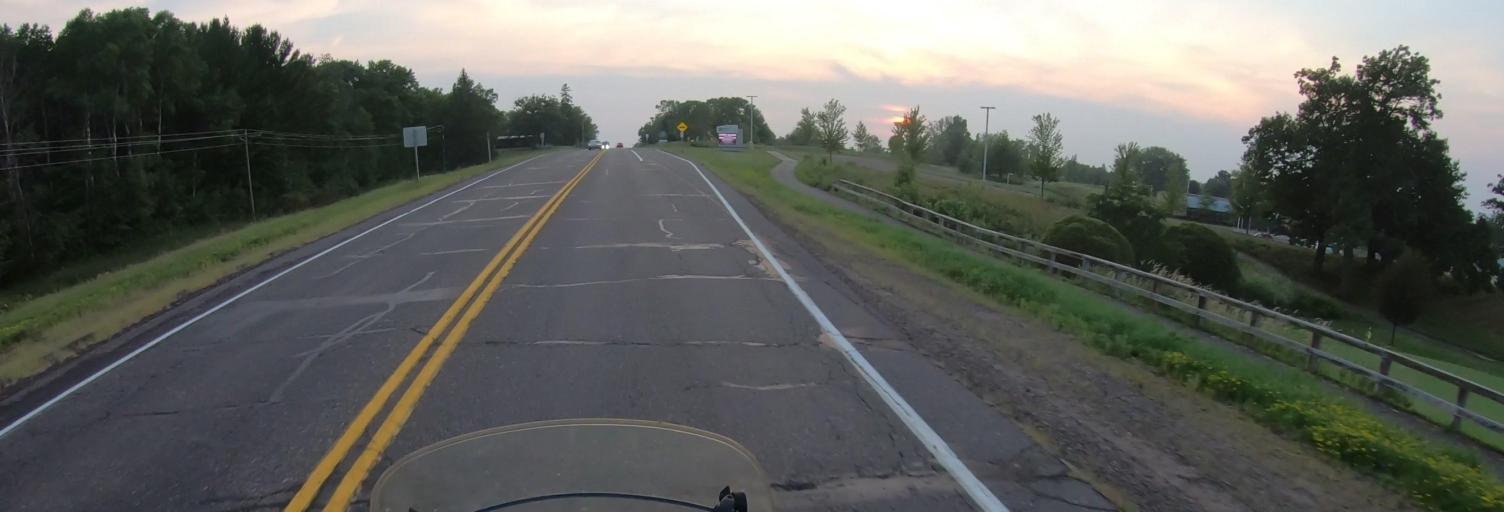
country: US
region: Wisconsin
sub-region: Burnett County
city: Grantsburg
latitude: 45.7730
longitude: -92.6853
